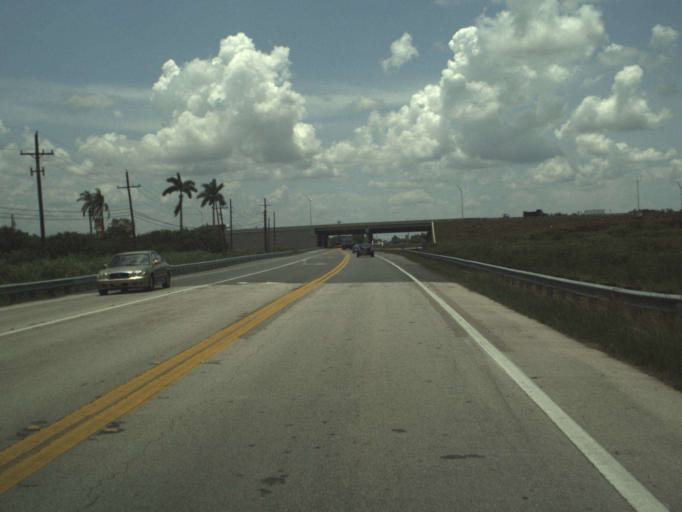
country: US
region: Florida
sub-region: Saint Lucie County
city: Lakewood Park
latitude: 27.4583
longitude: -80.3991
